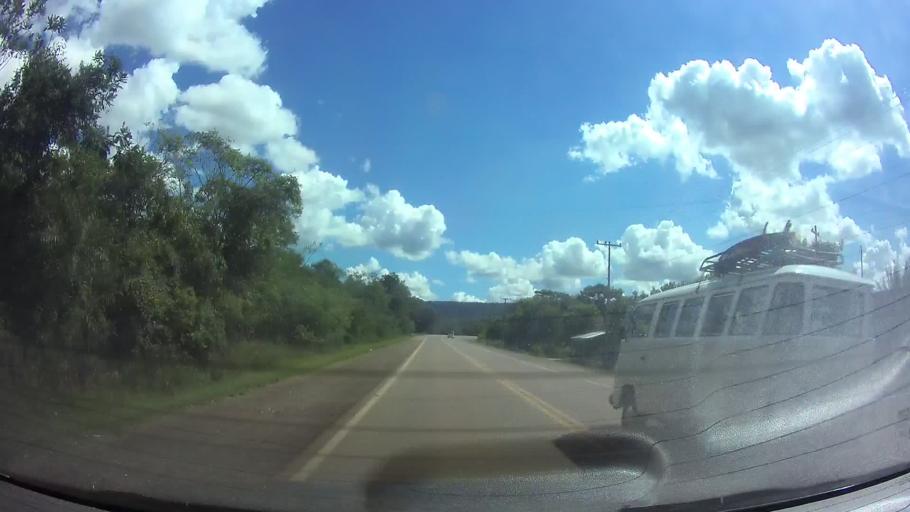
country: PY
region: Guaira
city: Itape
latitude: -25.9152
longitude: -56.7010
